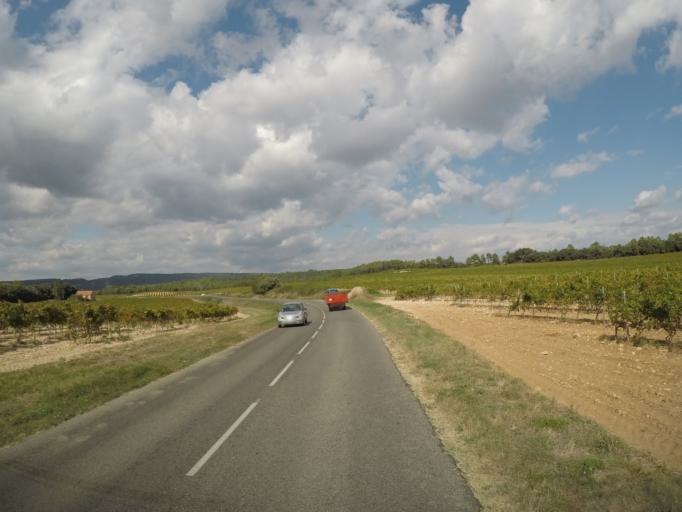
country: FR
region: Rhone-Alpes
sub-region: Departement de la Drome
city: Saint-Restitut
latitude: 44.3231
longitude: 4.8260
